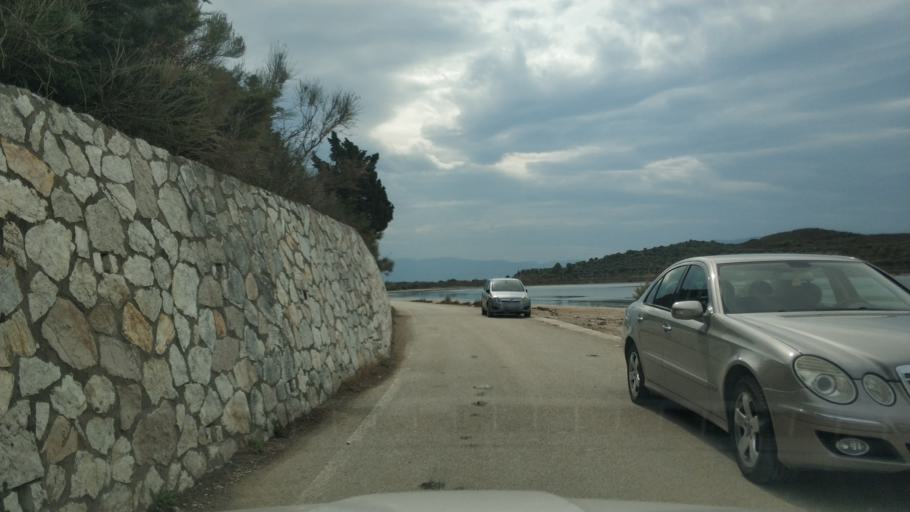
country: AL
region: Vlore
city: Vlore
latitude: 40.5172
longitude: 19.4065
